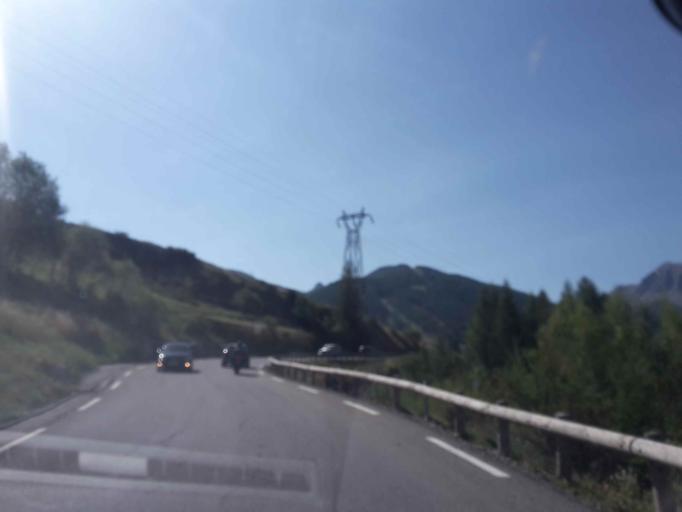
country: FR
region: Provence-Alpes-Cote d'Azur
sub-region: Departement des Hautes-Alpes
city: Guillestre
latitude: 44.6032
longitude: 6.6887
